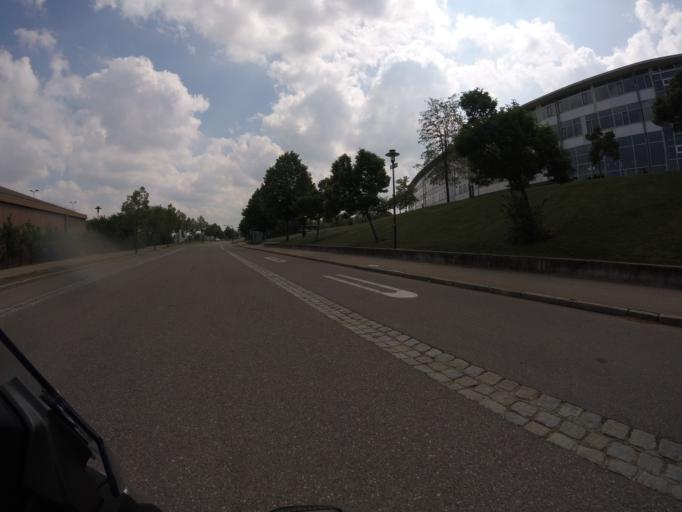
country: DE
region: Bavaria
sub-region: Upper Bavaria
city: Wolnzach
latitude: 48.5919
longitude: 11.6357
